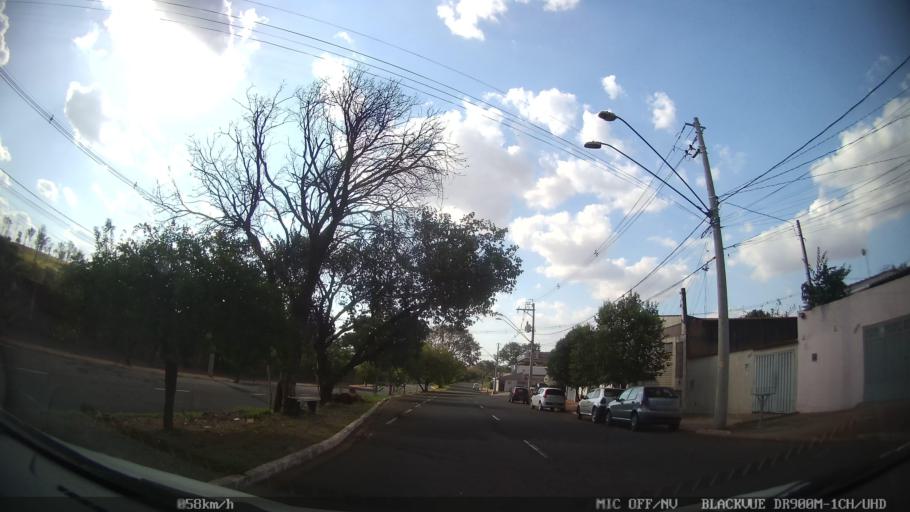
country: BR
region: Sao Paulo
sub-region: Ribeirao Preto
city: Ribeirao Preto
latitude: -21.1897
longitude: -47.8443
